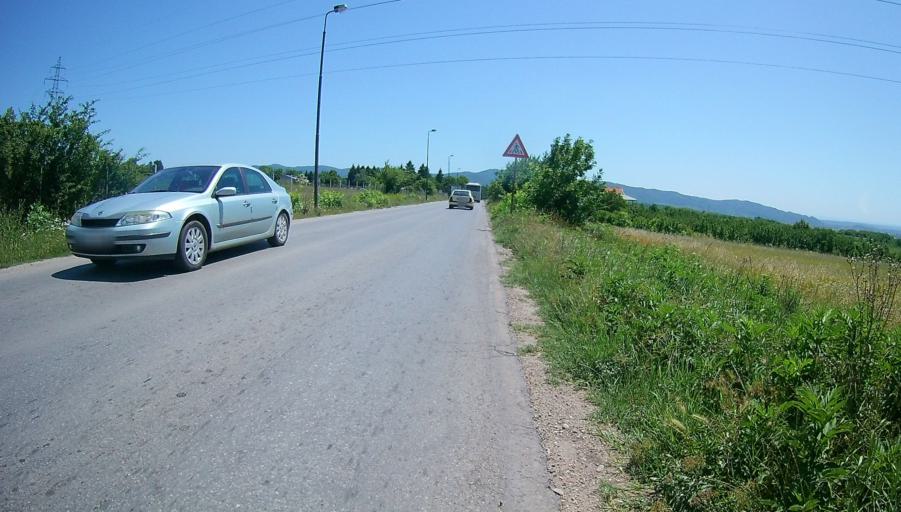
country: RS
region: Central Serbia
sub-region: Nisavski Okrug
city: Nis
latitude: 43.2971
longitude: 21.8786
